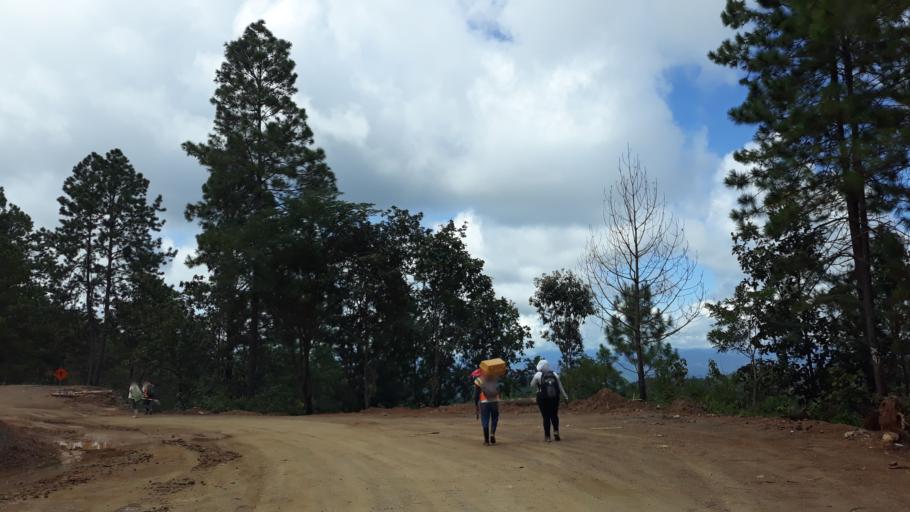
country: HN
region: El Paraiso
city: Santa Cruz
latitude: 13.7610
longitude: -86.6491
